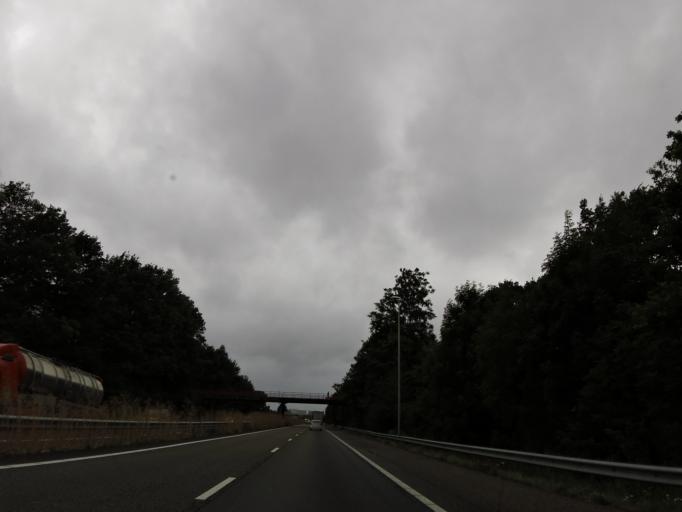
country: NL
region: Limburg
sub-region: Gemeente Beek
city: Beek
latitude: 50.9495
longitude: 5.8273
